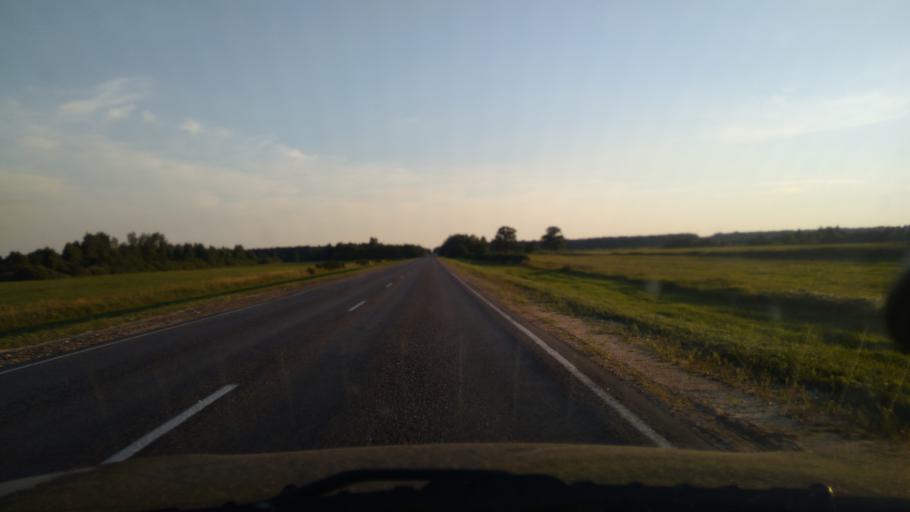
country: BY
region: Brest
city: Nyakhachava
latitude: 52.6214
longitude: 25.1600
